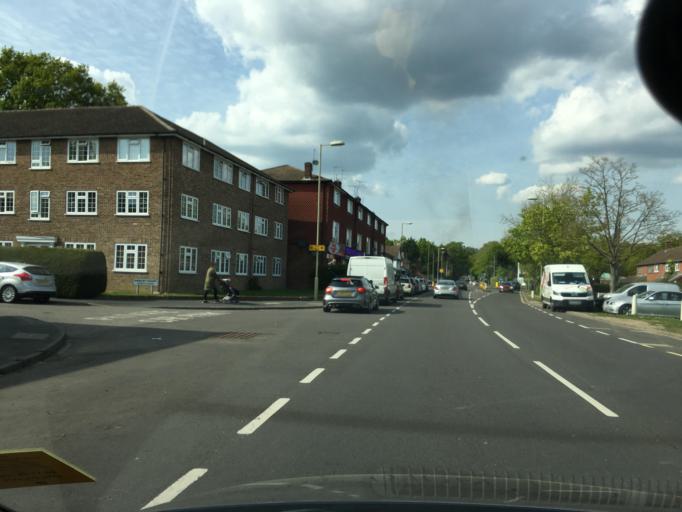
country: GB
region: England
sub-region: Hampshire
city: Farnborough
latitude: 51.3104
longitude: -0.7756
